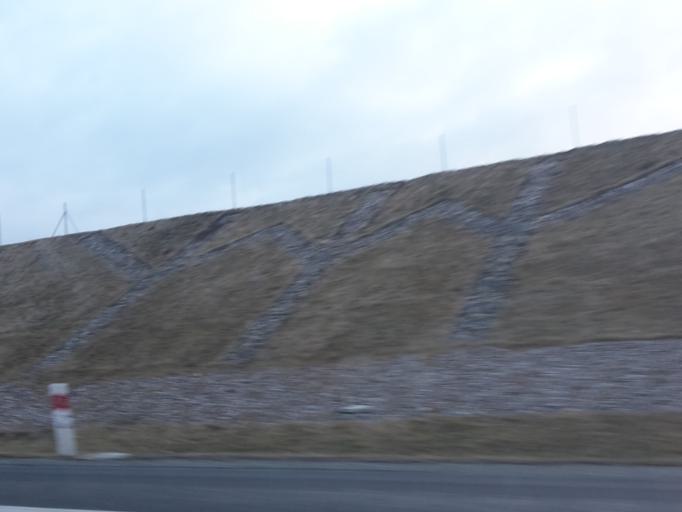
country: PL
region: Warmian-Masurian Voivodeship
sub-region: Powiat ostrodzki
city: Maldyty
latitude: 53.9522
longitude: 19.6957
